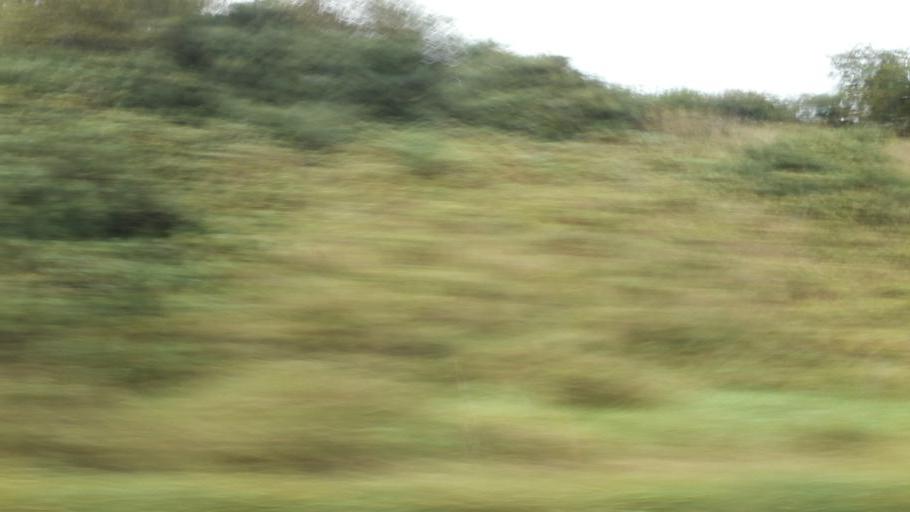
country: IE
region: Leinster
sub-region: An Longfort
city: Lanesborough
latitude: 53.7626
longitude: -8.0159
